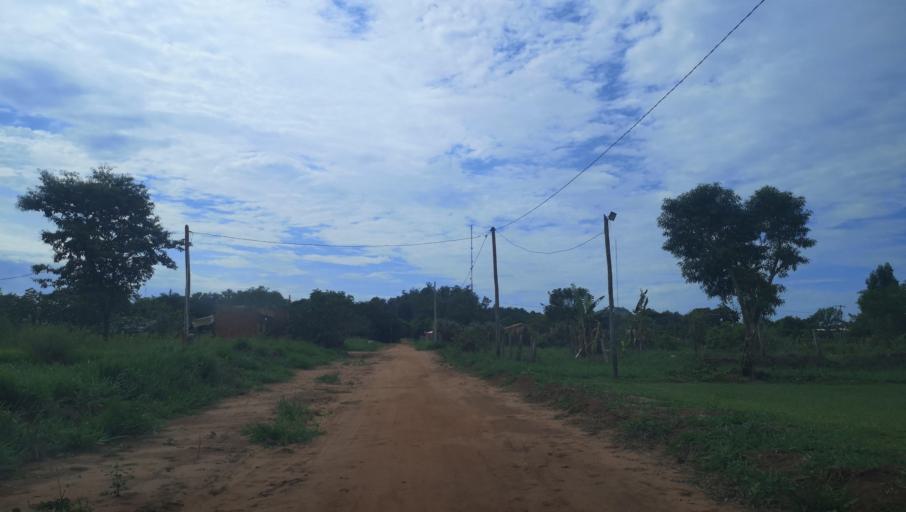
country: PY
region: San Pedro
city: Capiibary
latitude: -24.7238
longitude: -56.0215
